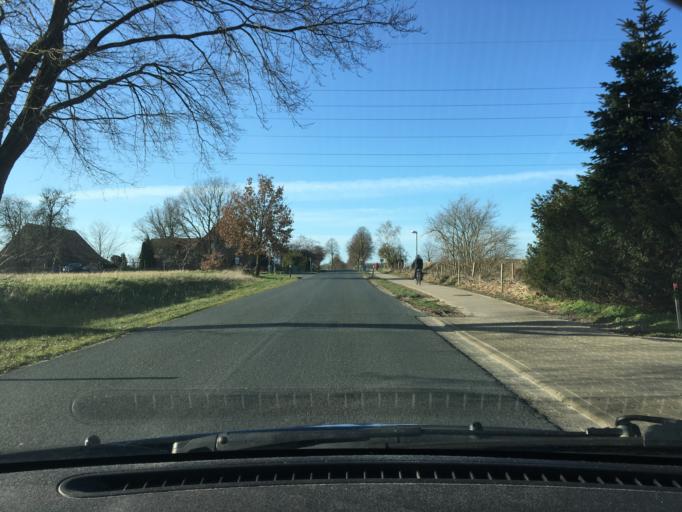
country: DE
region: Lower Saxony
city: Embsen
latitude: 53.2145
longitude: 10.3663
